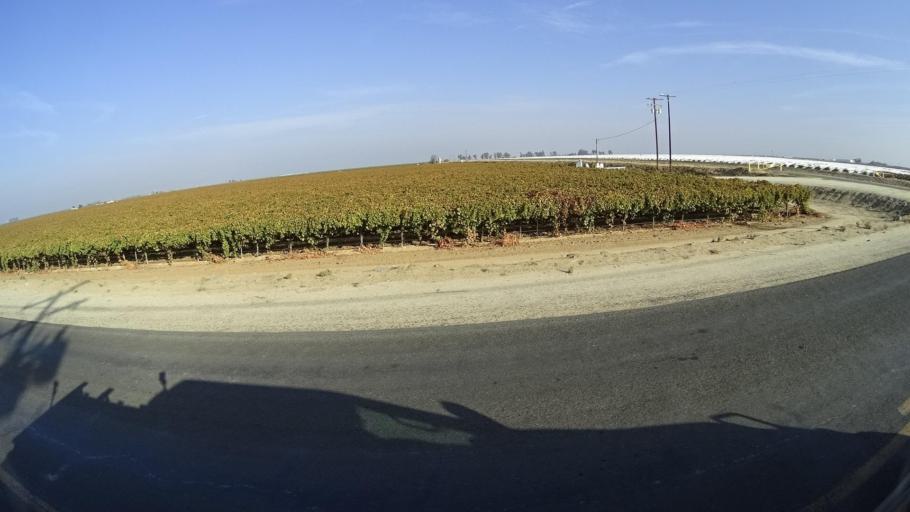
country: US
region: California
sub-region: Kern County
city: McFarland
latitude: 35.6746
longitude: -119.1964
